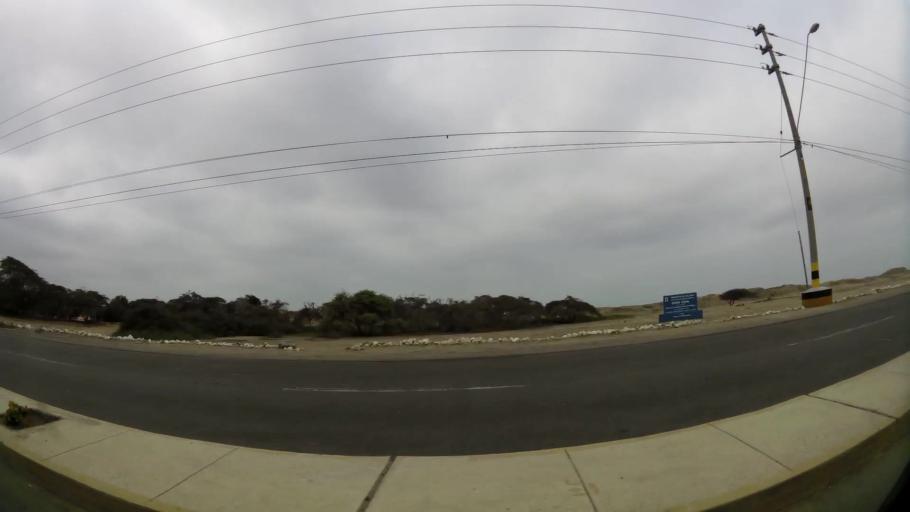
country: PE
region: La Libertad
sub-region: Provincia de Trujillo
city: La Esperanza
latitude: -8.0991
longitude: -79.0673
